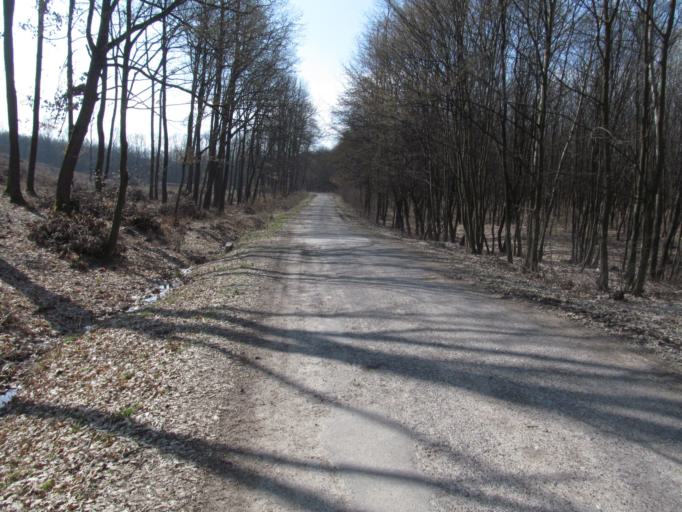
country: HU
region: Borsod-Abauj-Zemplen
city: Putnok
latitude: 48.3463
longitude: 20.4379
